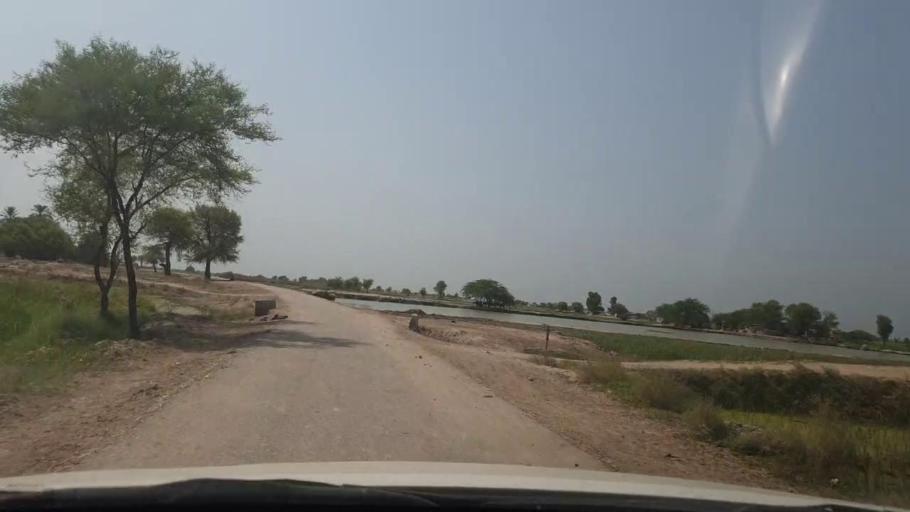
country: PK
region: Sindh
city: Shikarpur
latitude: 28.0065
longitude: 68.7129
